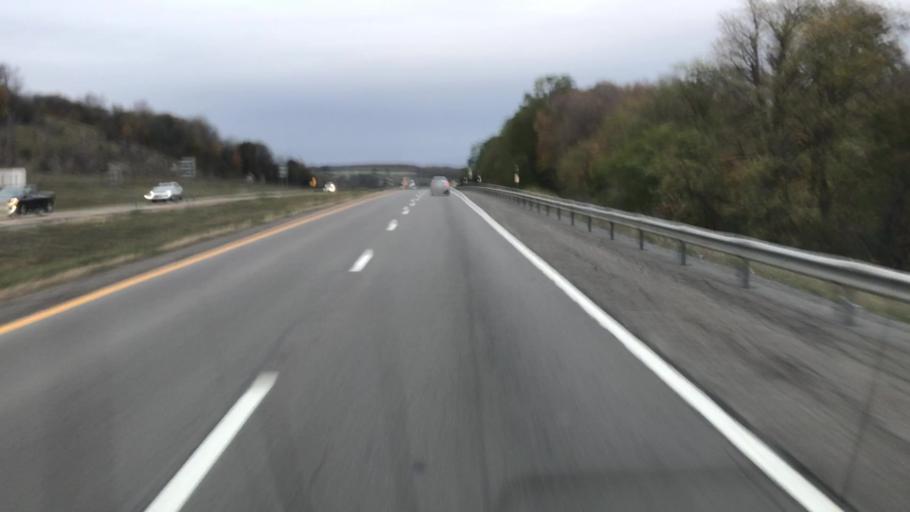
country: US
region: New York
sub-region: Onondaga County
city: Camillus
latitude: 43.0381
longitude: -76.3191
